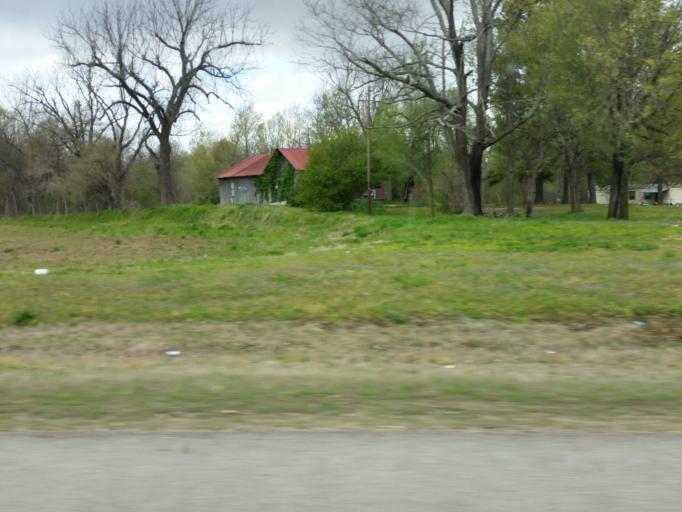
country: US
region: Arkansas
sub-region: Clay County
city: Corning
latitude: 36.4742
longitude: -90.5591
